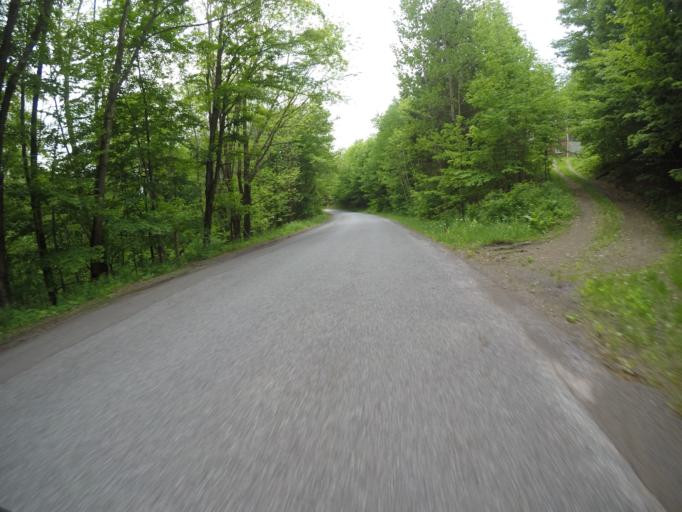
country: US
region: New York
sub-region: Delaware County
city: Stamford
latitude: 42.2444
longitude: -74.7100
